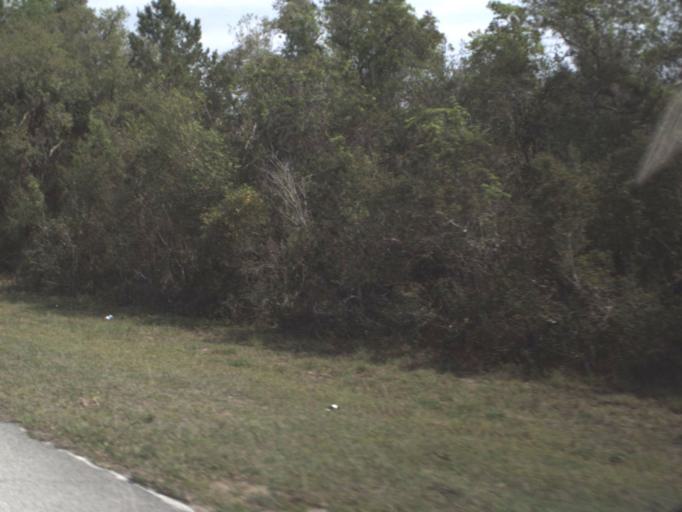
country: US
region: Florida
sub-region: Lake County
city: Astor
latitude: 29.2254
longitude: -81.6461
